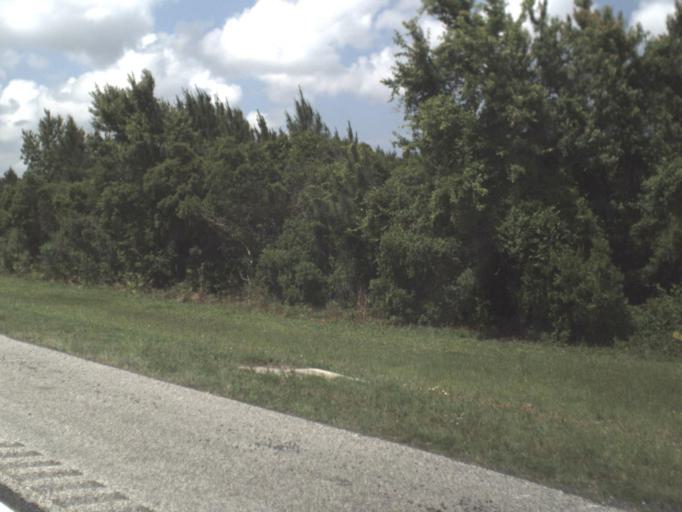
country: US
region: Florida
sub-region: Saint Johns County
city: Saint Augustine Shores
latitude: 29.7341
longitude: -81.3408
